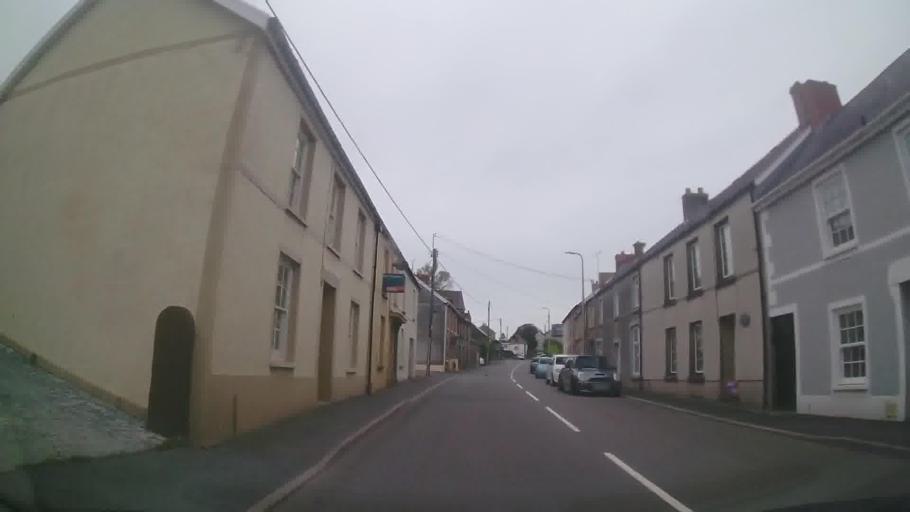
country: GB
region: Wales
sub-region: Carmarthenshire
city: Saint Clears
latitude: 51.8141
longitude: -4.4964
